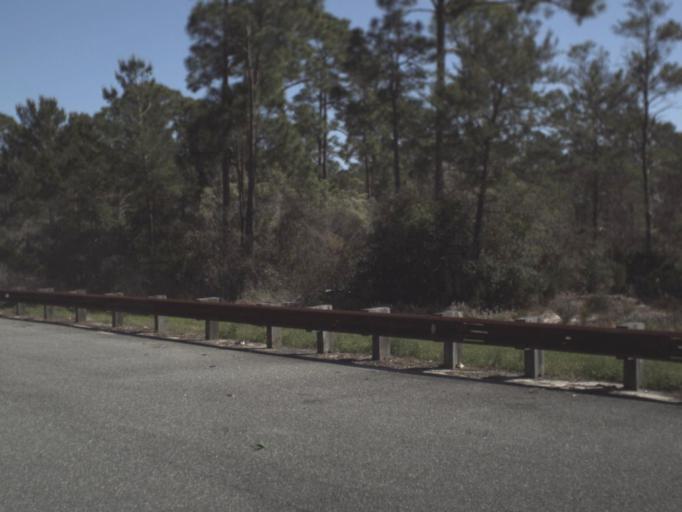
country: US
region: Florida
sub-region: Gulf County
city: Port Saint Joe
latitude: 29.8884
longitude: -85.3508
